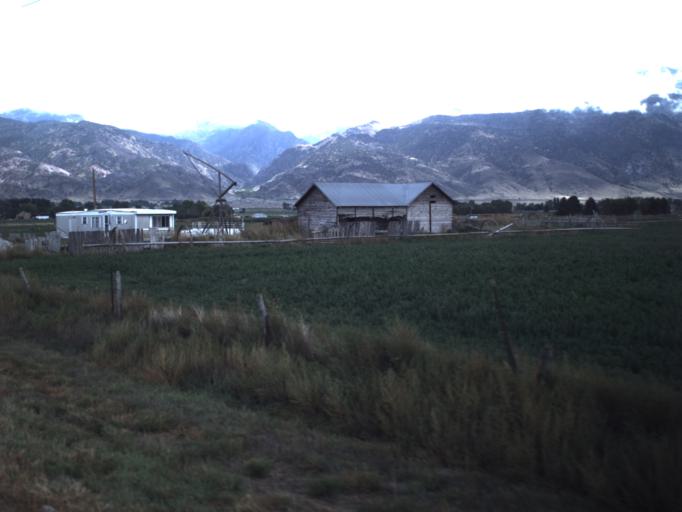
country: US
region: Utah
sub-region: Sevier County
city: Monroe
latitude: 38.6290
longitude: -112.1497
